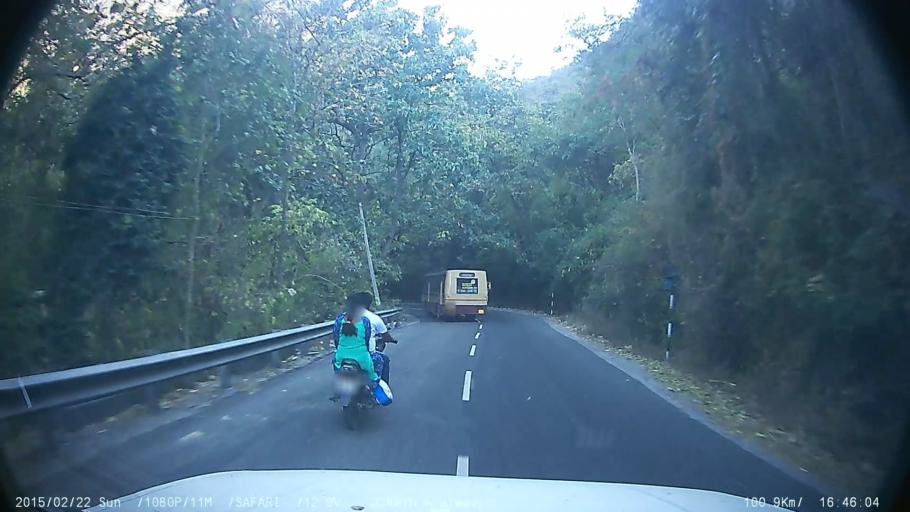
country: IN
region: Tamil Nadu
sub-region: Theni
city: Gudalur
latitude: 9.6211
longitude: 77.1903
